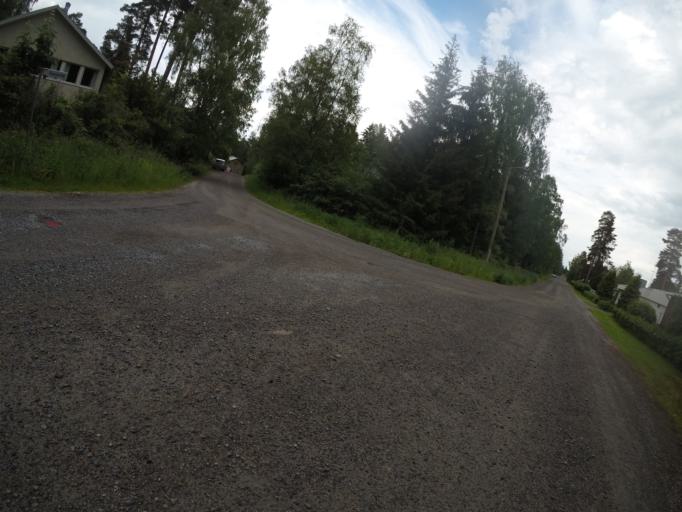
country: FI
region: Haeme
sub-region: Haemeenlinna
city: Haemeenlinna
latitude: 61.0129
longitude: 24.4883
